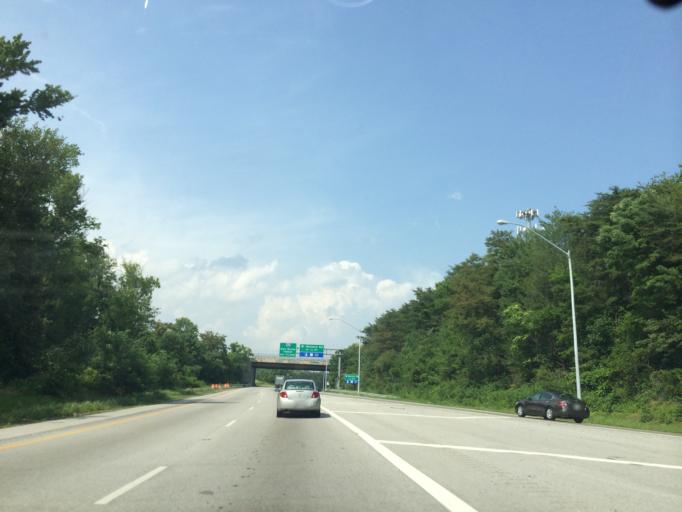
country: US
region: Maryland
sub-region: Howard County
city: Elkridge
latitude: 39.2033
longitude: -76.6909
